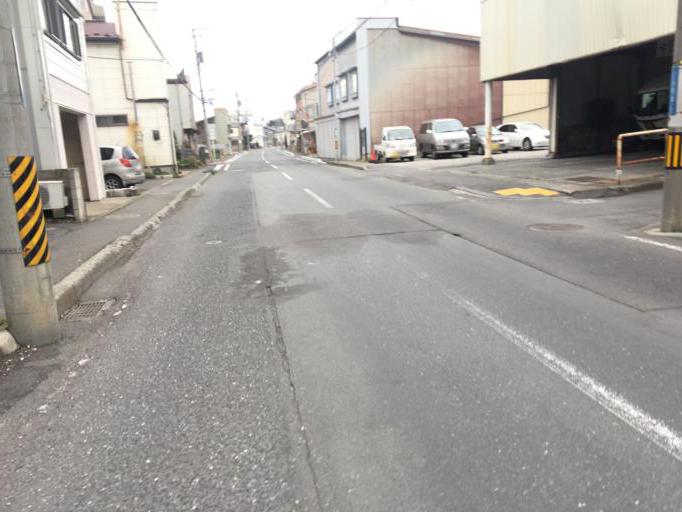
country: JP
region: Aomori
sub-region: Hachinohe Shi
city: Uchimaru
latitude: 40.5216
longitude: 141.5191
